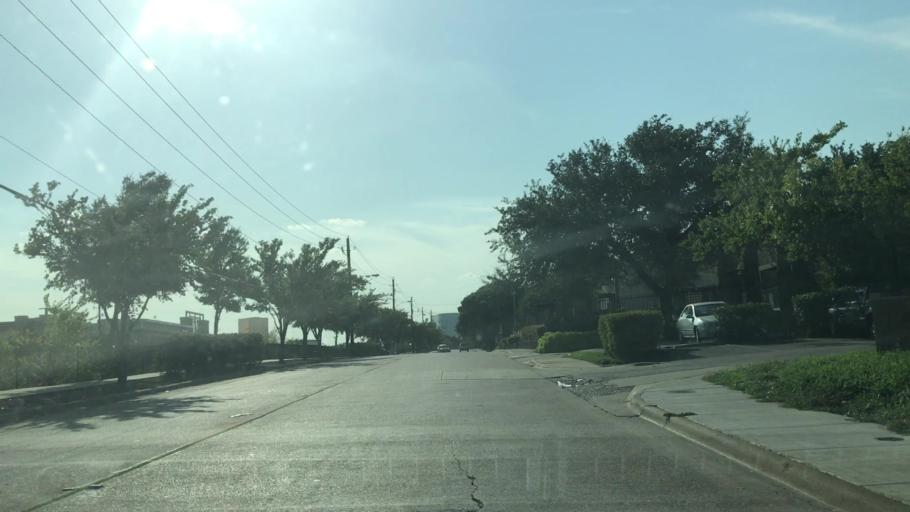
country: US
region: Texas
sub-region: Dallas County
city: Highland Park
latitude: 32.8640
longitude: -96.7514
